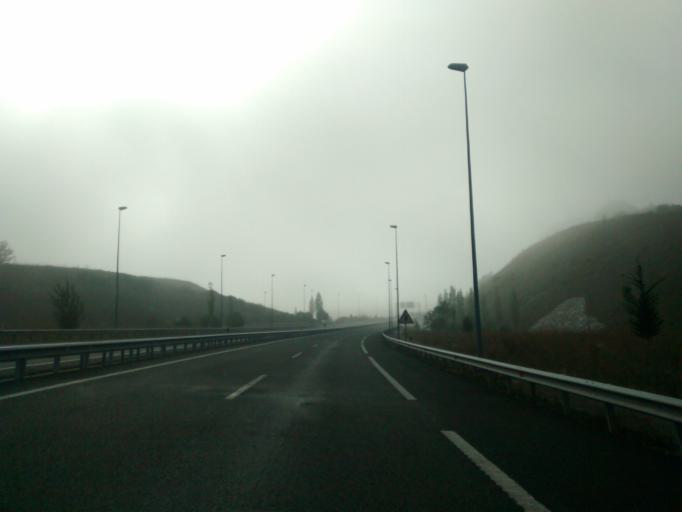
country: ES
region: Cantabria
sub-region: Provincia de Cantabria
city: Arenas de Iguna
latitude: 43.1843
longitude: -4.0597
